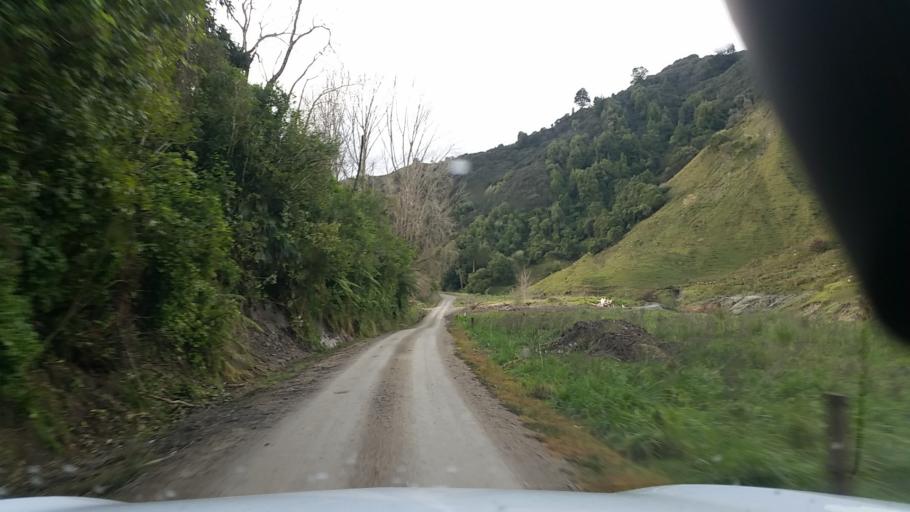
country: NZ
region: Taranaki
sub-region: South Taranaki District
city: Patea
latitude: -39.5695
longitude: 174.8096
